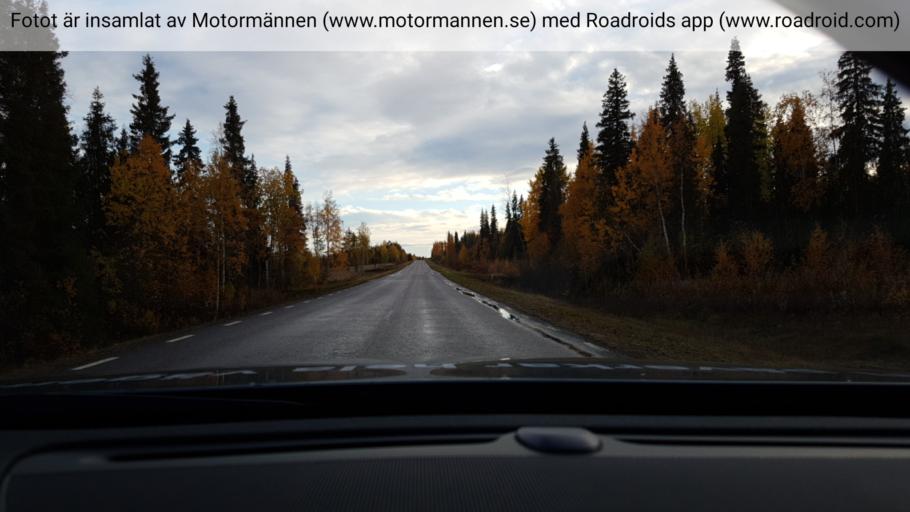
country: SE
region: Norrbotten
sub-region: Overkalix Kommun
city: OEverkalix
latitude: 66.8947
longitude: 22.7718
